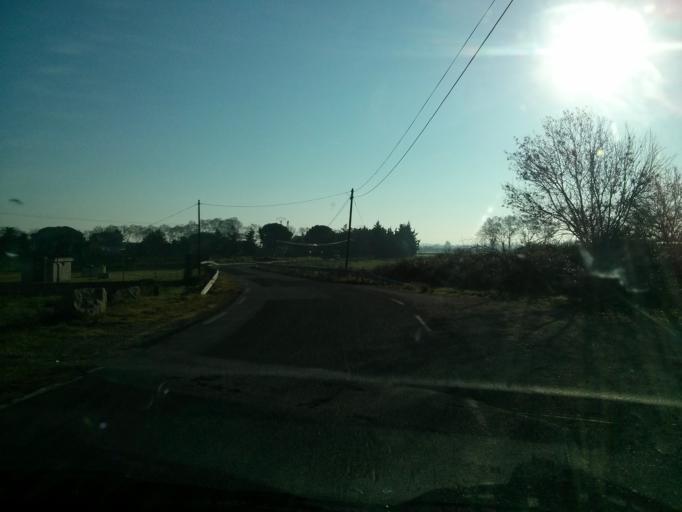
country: FR
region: Languedoc-Roussillon
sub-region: Departement du Gard
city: Mus
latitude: 43.7220
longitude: 4.2025
